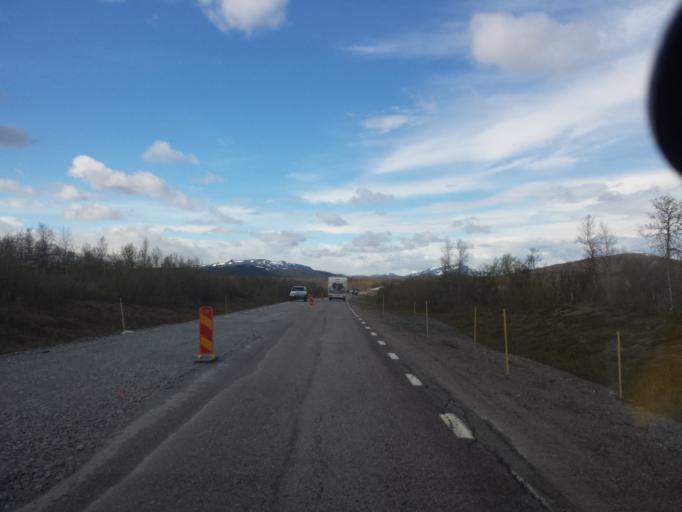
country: SE
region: Norrbotten
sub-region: Kiruna Kommun
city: Kiruna
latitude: 68.0101
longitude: 19.8450
